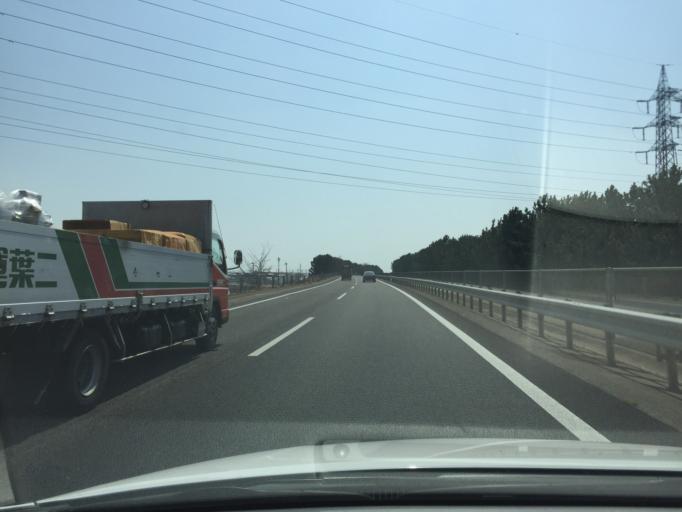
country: JP
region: Miyagi
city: Sendai-shi
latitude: 38.2362
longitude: 140.9524
